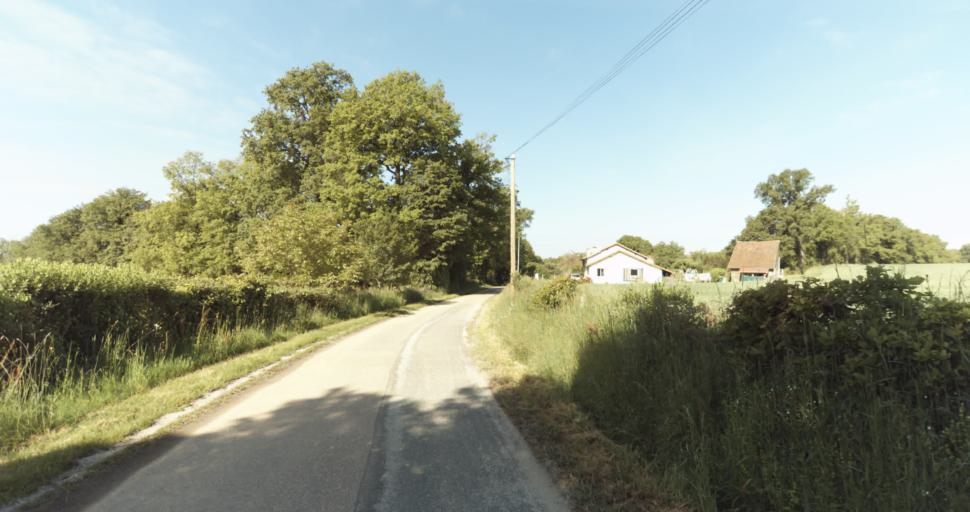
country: FR
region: Limousin
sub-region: Departement de la Haute-Vienne
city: Solignac
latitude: 45.7040
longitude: 1.2612
